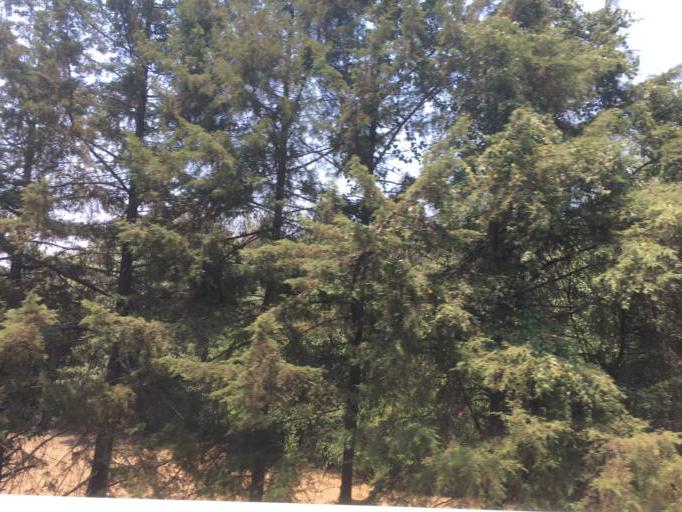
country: MX
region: Michoacan
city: Quiroga
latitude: 19.6380
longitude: -101.4791
